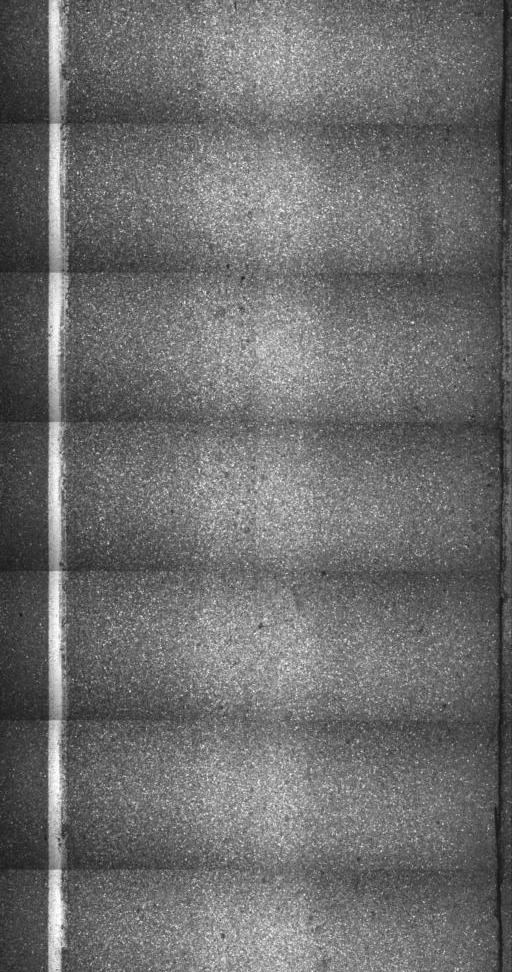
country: US
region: Vermont
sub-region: Rutland County
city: Fair Haven
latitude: 43.6807
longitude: -73.2892
